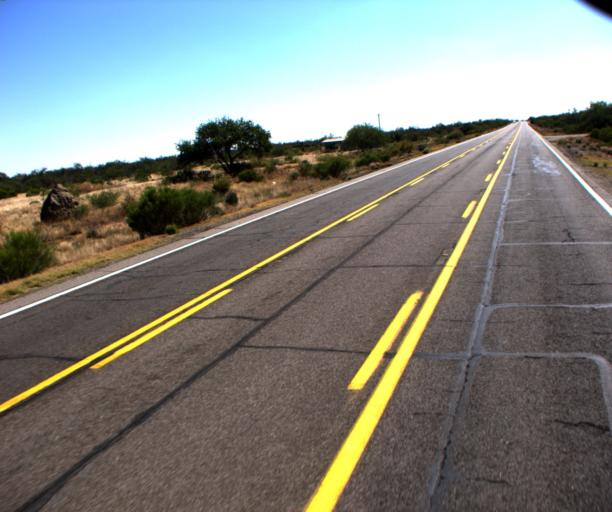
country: US
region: Arizona
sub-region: Pinal County
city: Oracle
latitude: 32.6180
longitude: -110.8144
